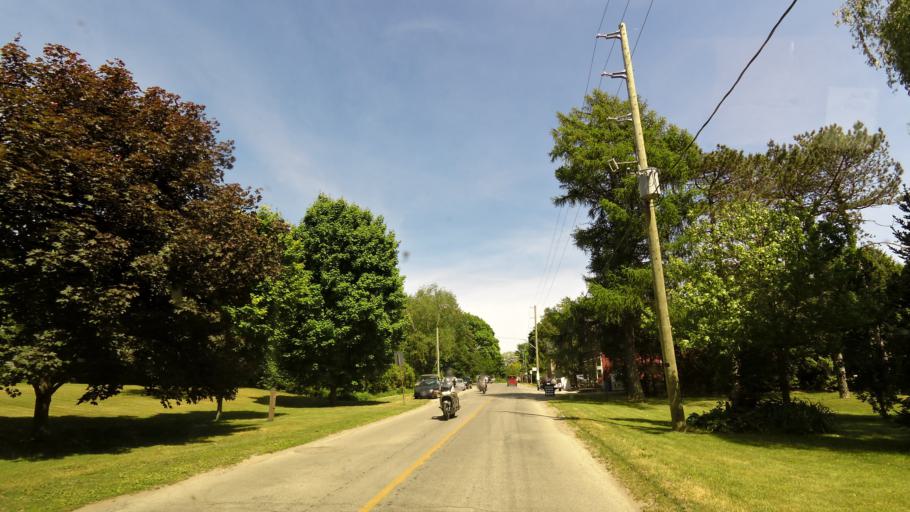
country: CA
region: Ontario
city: Norfolk County
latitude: 42.7109
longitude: -80.3132
